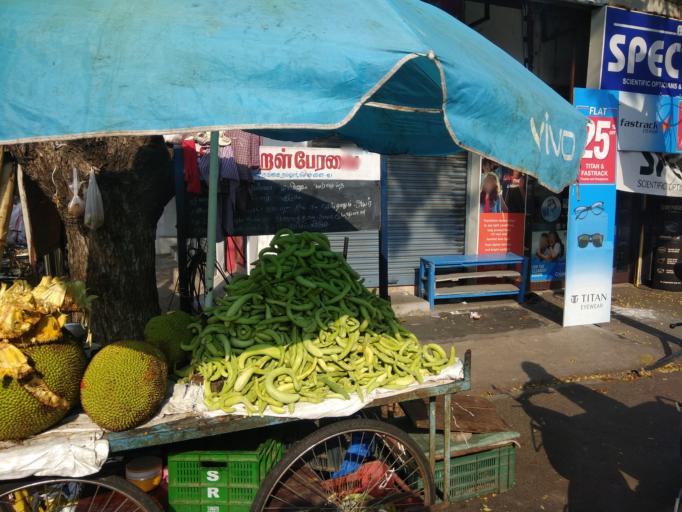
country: IN
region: Tamil Nadu
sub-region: Kancheepuram
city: Saint Thomas Mount
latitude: 12.9848
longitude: 80.1885
